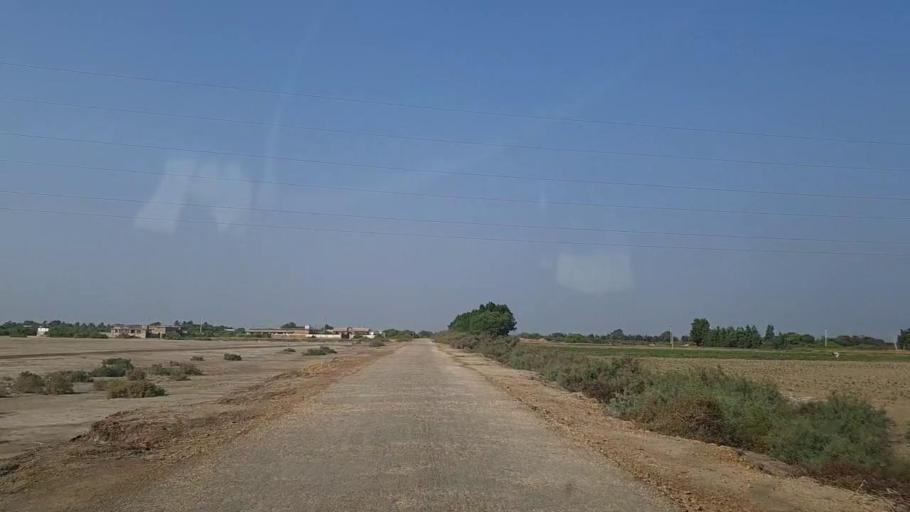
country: PK
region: Sindh
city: Mirpur Sakro
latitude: 24.5664
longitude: 67.6857
